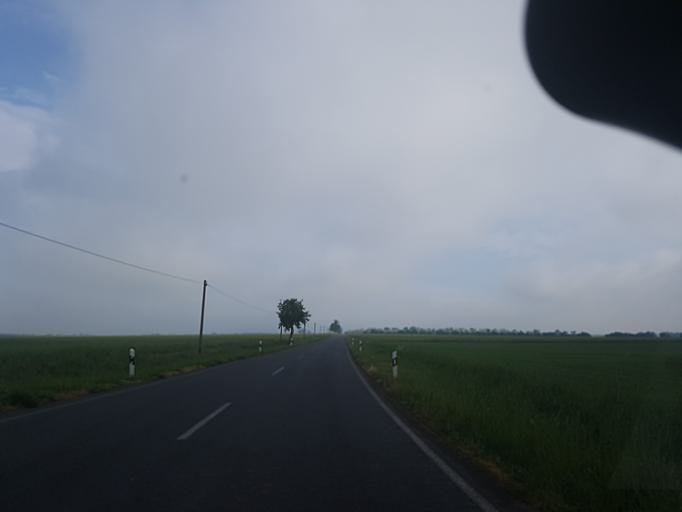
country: DE
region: Saxony-Anhalt
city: Rodleben
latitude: 51.9937
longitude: 12.2312
